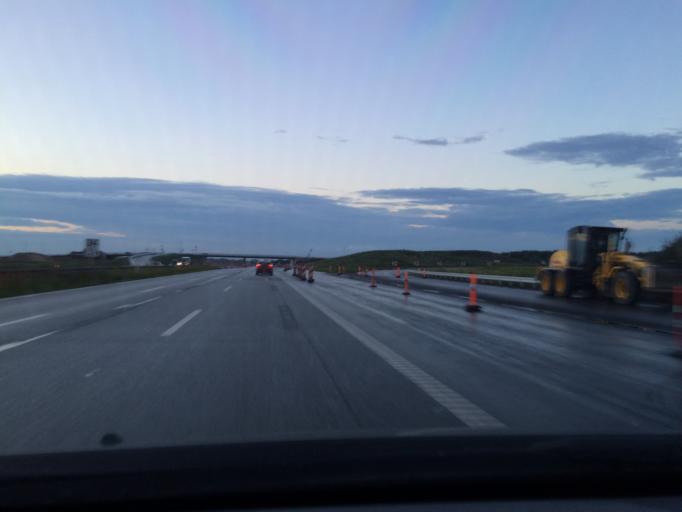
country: DK
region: Zealand
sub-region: Solrod Kommune
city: Solrod
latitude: 55.5019
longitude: 12.1749
